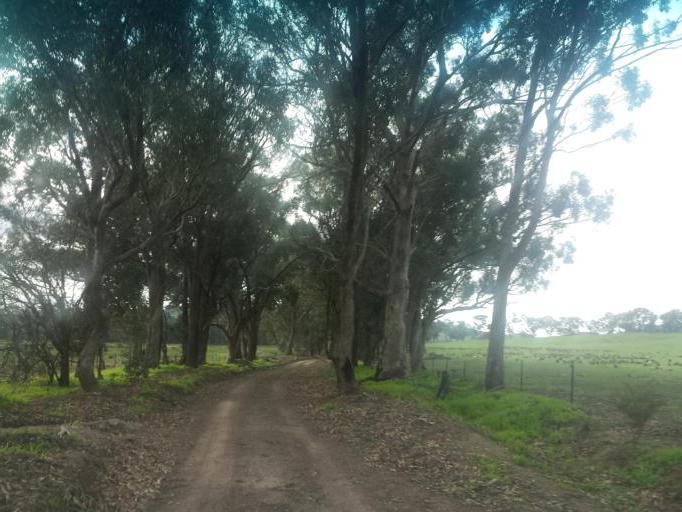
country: AU
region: Victoria
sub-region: Murrindindi
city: Kinglake West
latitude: -37.0187
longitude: 145.2502
